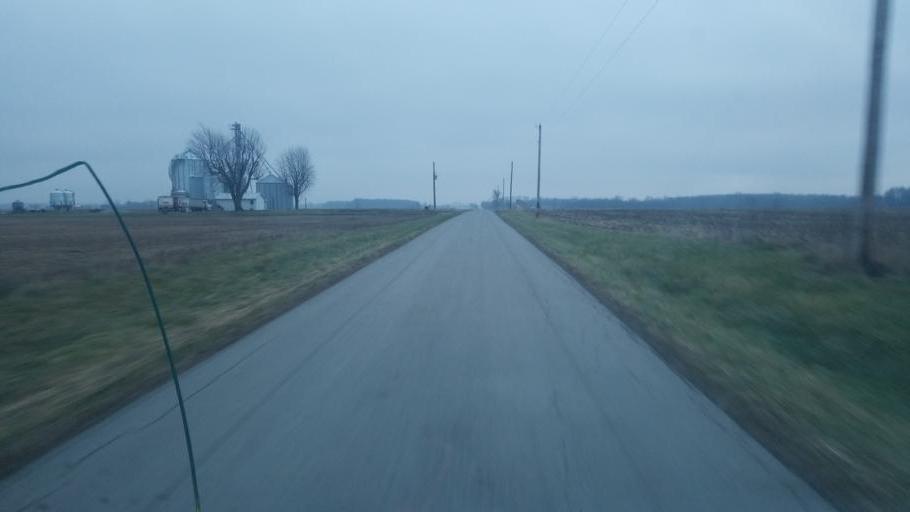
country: US
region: Ohio
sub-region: Seneca County
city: Tiffin
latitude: 40.9784
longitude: -83.1319
